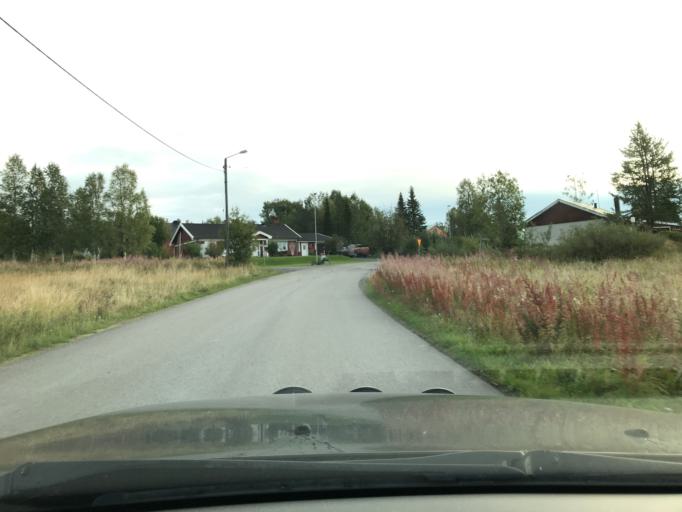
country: SE
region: Norrbotten
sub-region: Gallivare Kommun
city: Malmberget
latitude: 67.6462
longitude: 21.0627
